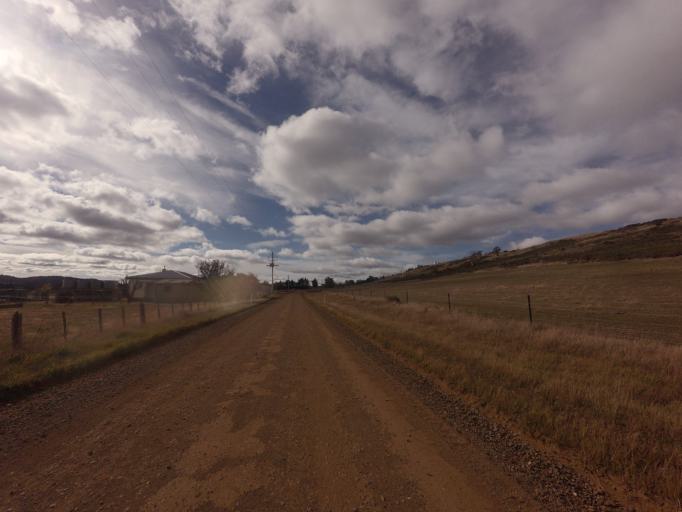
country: AU
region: Tasmania
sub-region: Brighton
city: Bridgewater
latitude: -42.4177
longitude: 147.3940
